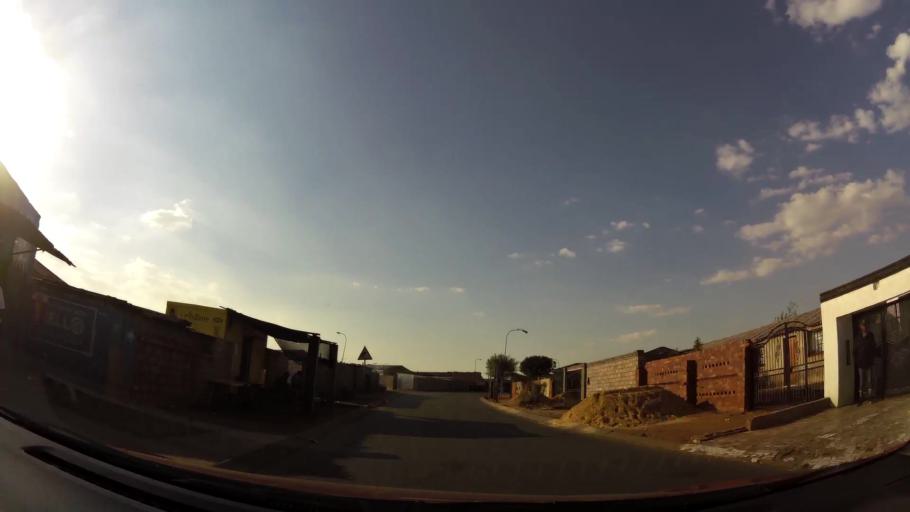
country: ZA
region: Gauteng
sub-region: City of Johannesburg Metropolitan Municipality
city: Soweto
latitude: -26.2271
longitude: 27.8957
